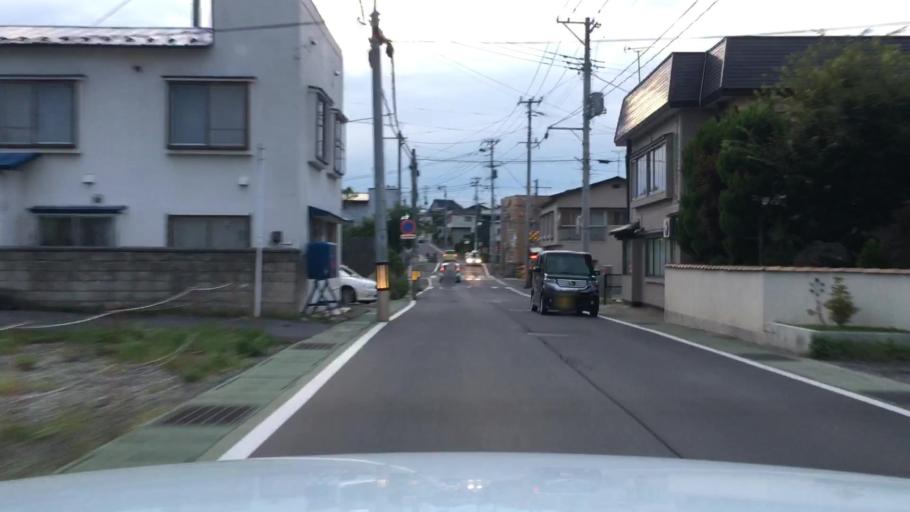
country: JP
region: Aomori
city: Hirosaki
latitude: 40.5924
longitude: 140.4691
